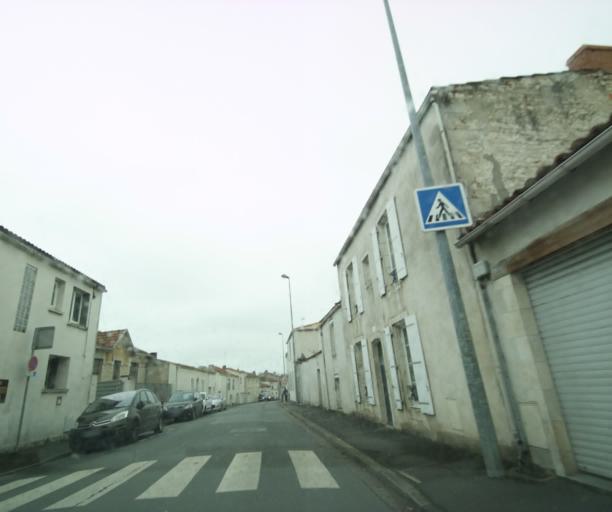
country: FR
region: Poitou-Charentes
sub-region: Departement de la Charente-Maritime
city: La Rochelle
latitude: 46.1762
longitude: -1.1395
